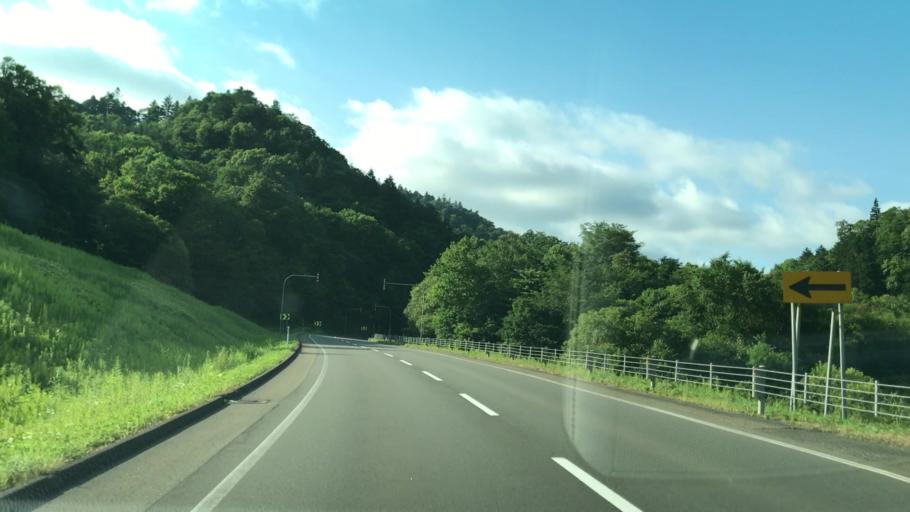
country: JP
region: Hokkaido
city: Chitose
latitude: 42.8850
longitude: 142.1234
